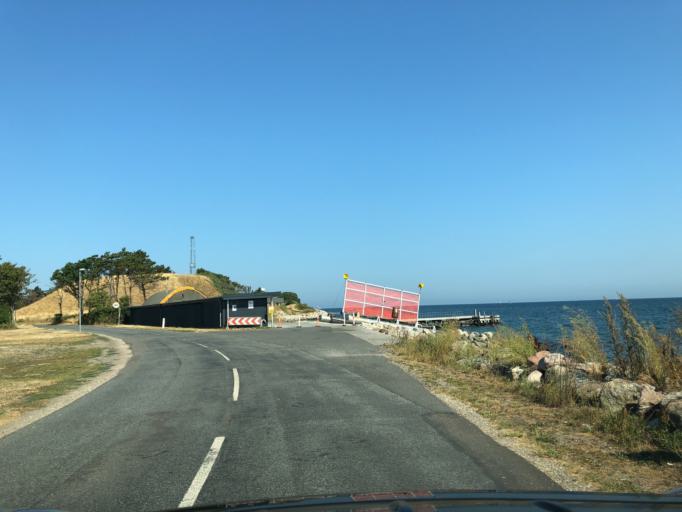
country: DK
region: Zealand
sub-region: Odsherred Kommune
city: Asnaes
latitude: 56.0041
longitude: 11.2841
